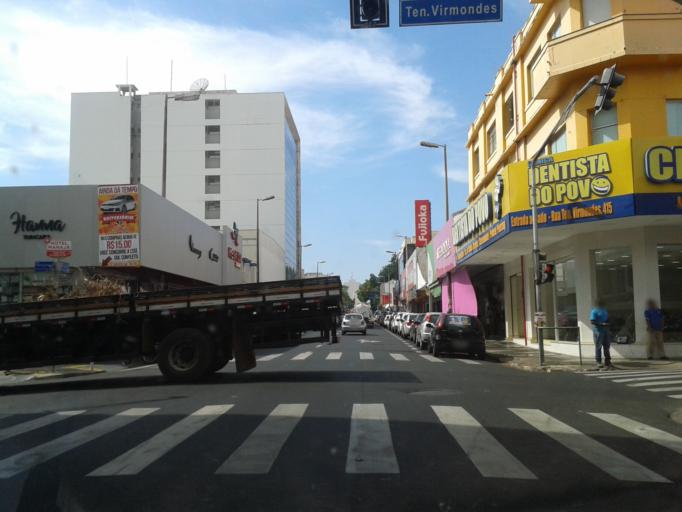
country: BR
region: Minas Gerais
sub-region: Uberlandia
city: Uberlandia
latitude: -18.9178
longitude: -48.2774
